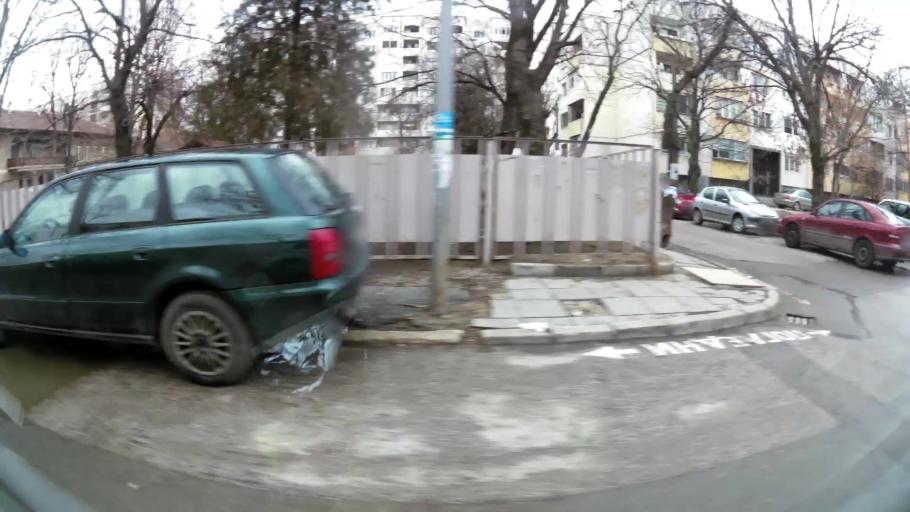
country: BG
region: Sofia-Capital
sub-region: Stolichna Obshtina
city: Sofia
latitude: 42.7258
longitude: 23.3012
